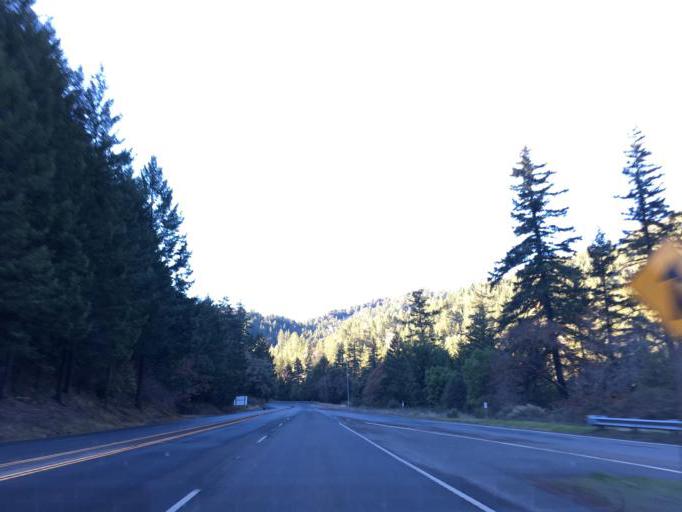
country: US
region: California
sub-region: Mendocino County
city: Laytonville
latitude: 39.8269
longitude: -123.5959
